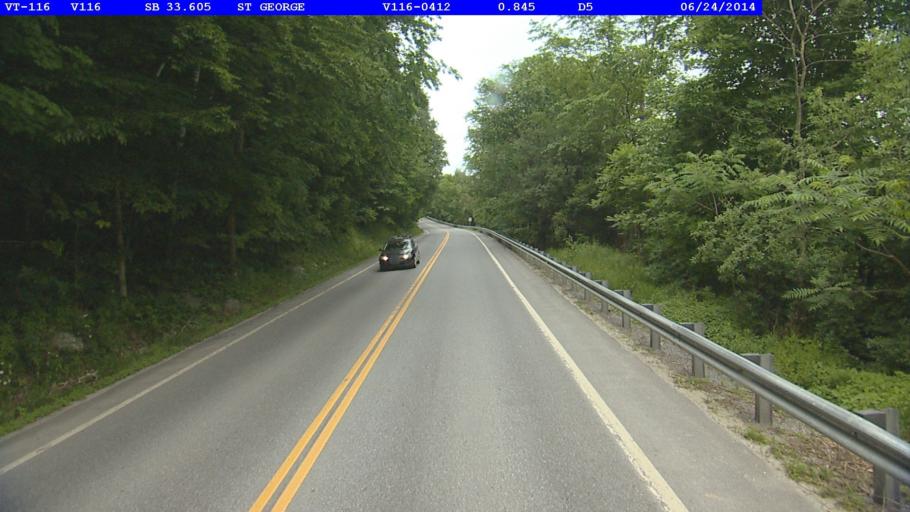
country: US
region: Vermont
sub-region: Chittenden County
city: Hinesburg
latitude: 44.3754
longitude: -73.1347
